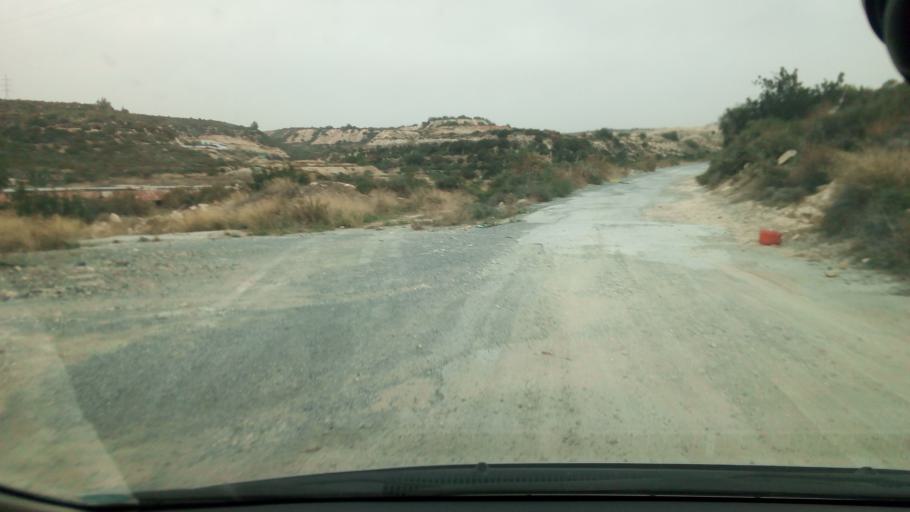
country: CY
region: Limassol
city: Ypsonas
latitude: 34.7185
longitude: 32.9539
